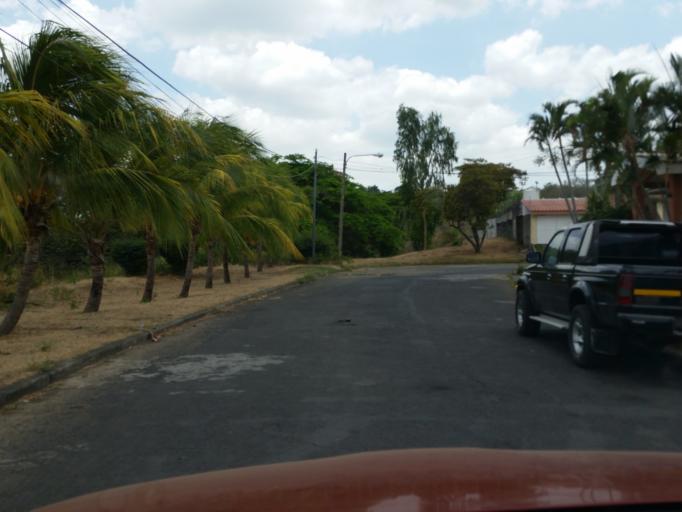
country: NI
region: Managua
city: Managua
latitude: 12.0835
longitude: -86.2432
